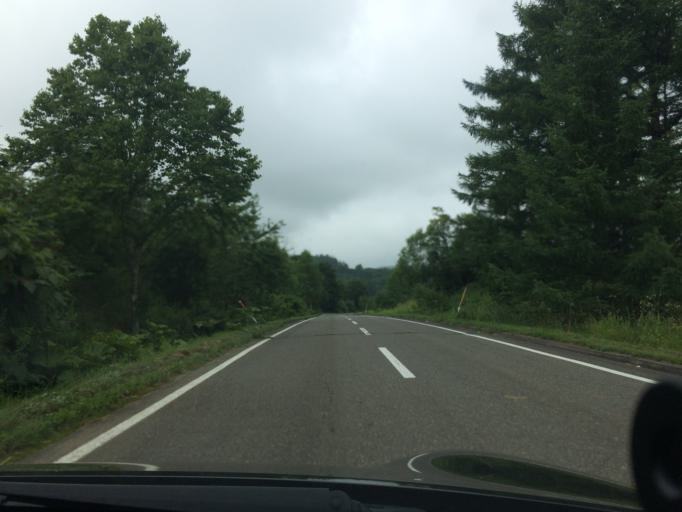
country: JP
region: Hokkaido
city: Otofuke
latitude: 43.0004
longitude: 143.0836
